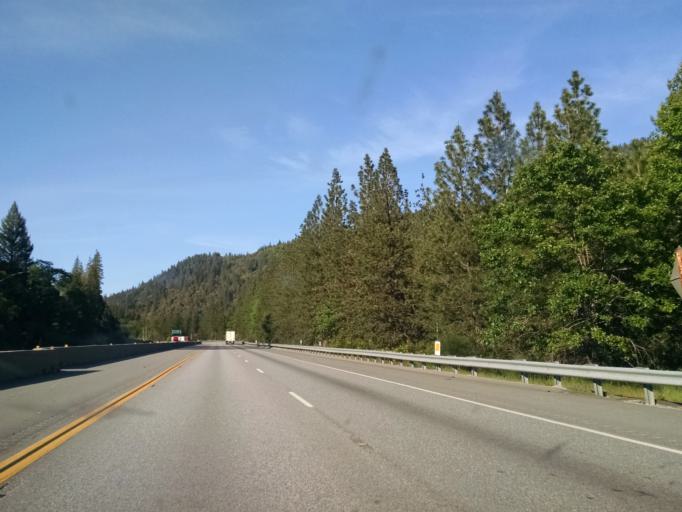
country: US
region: California
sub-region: Siskiyou County
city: Dunsmuir
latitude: 41.0203
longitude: -122.4004
